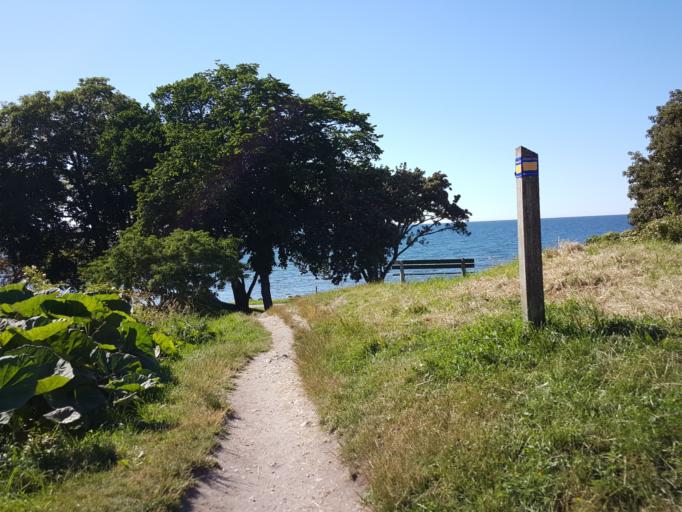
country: SE
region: Gotland
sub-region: Gotland
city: Visby
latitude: 57.6469
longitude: 18.2968
